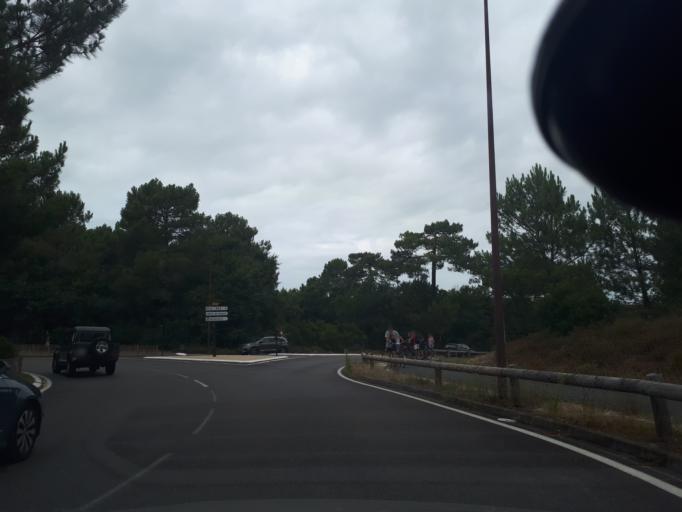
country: FR
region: Aquitaine
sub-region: Departement de la Gironde
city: Arcachon
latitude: 44.5986
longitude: -1.1964
